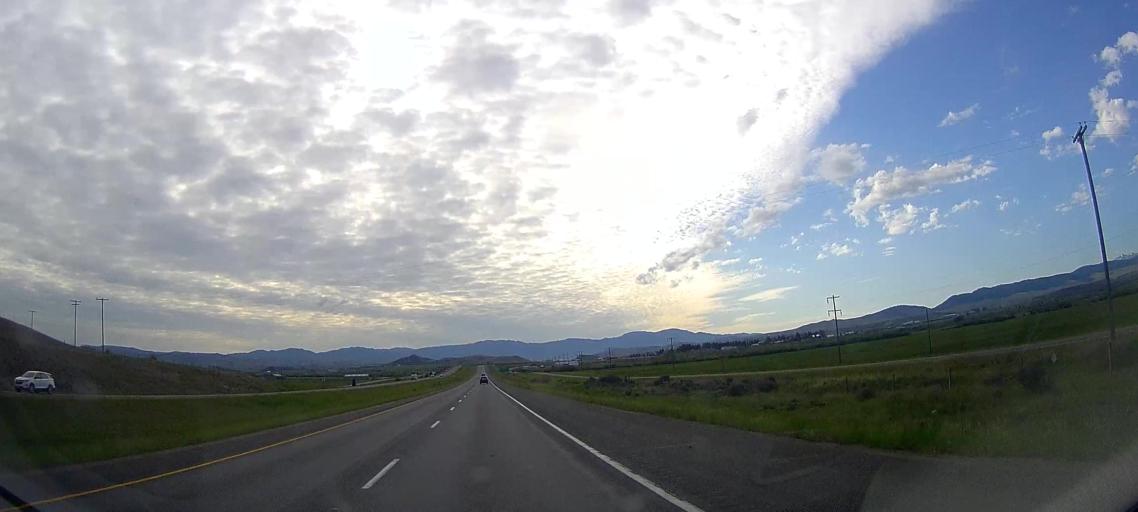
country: US
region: Montana
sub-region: Silver Bow County
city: Butte-Silver Bow (Balance)
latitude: 46.0098
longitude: -112.7022
